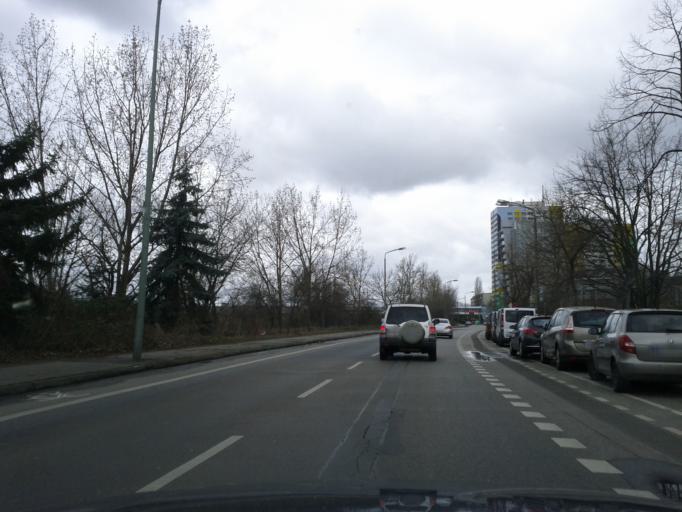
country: DE
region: Berlin
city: Fennpfuhl
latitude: 52.5233
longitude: 13.4694
